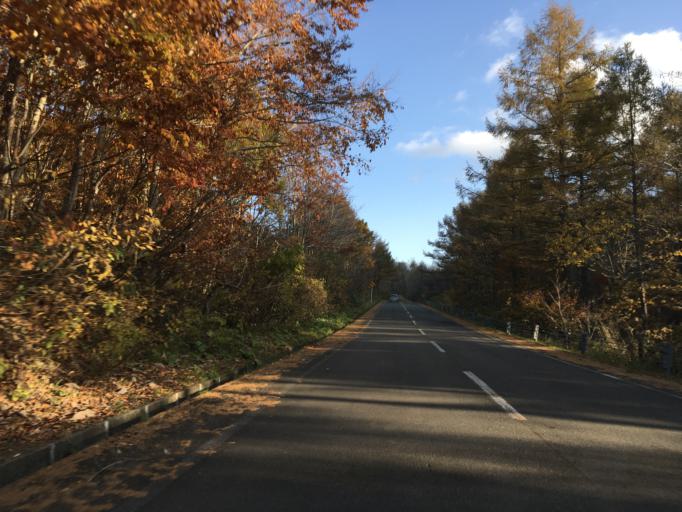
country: JP
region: Akita
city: Yuzawa
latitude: 39.0090
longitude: 140.7242
